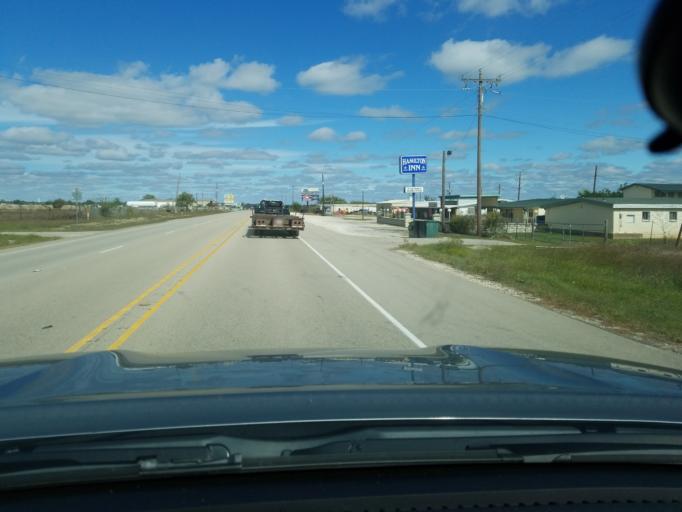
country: US
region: Texas
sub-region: Hamilton County
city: Hamilton
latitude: 31.6758
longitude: -98.1353
